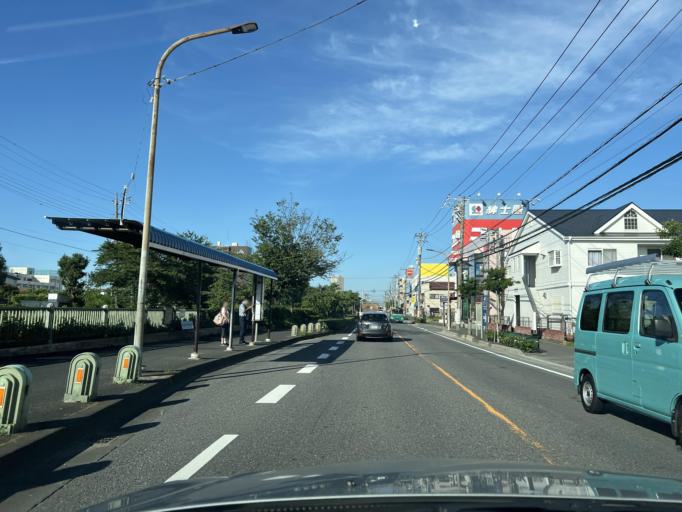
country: JP
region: Chiba
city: Funabashi
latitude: 35.7346
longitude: 139.9464
